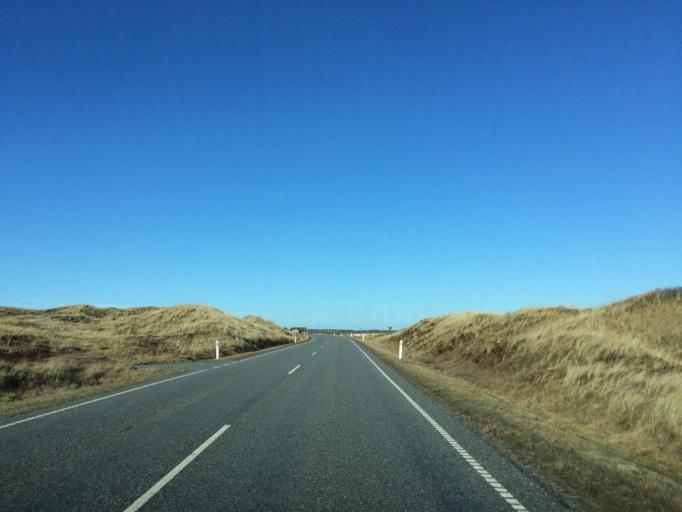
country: DK
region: Central Jutland
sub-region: Ringkobing-Skjern Kommune
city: Ringkobing
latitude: 56.2059
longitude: 8.1326
